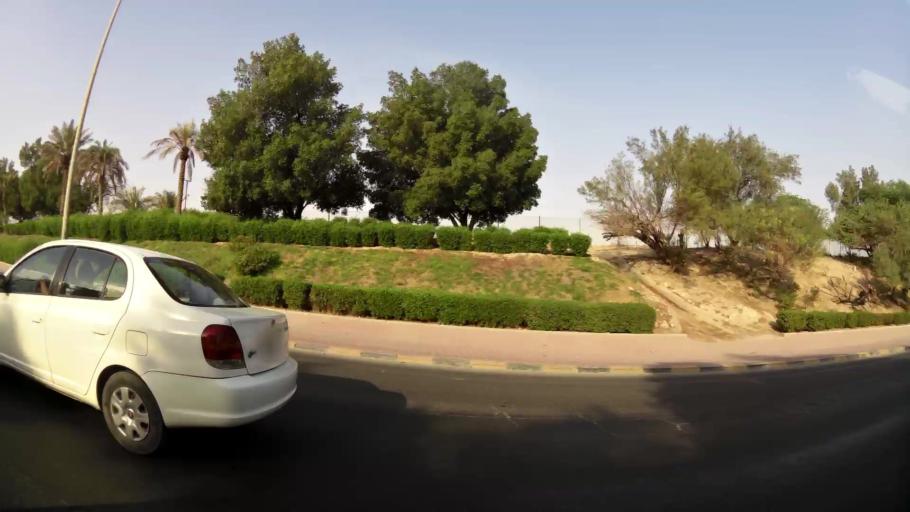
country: KW
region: Al Farwaniyah
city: Janub as Surrah
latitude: 29.2539
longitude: 47.9887
